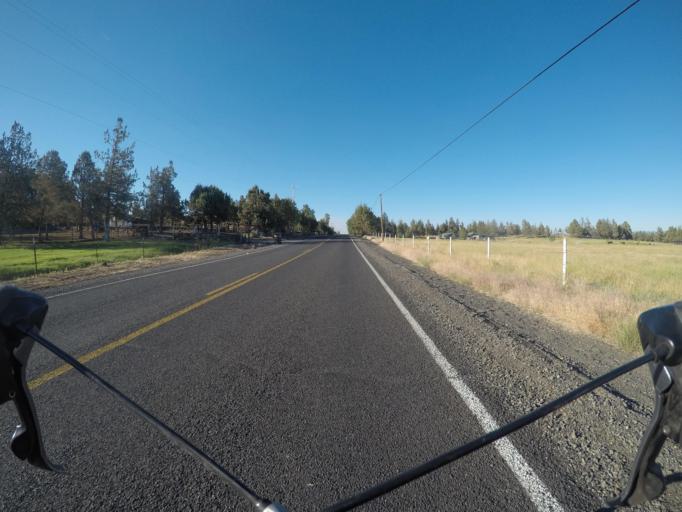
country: US
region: Oregon
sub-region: Deschutes County
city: Redmond
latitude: 44.2572
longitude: -121.2395
